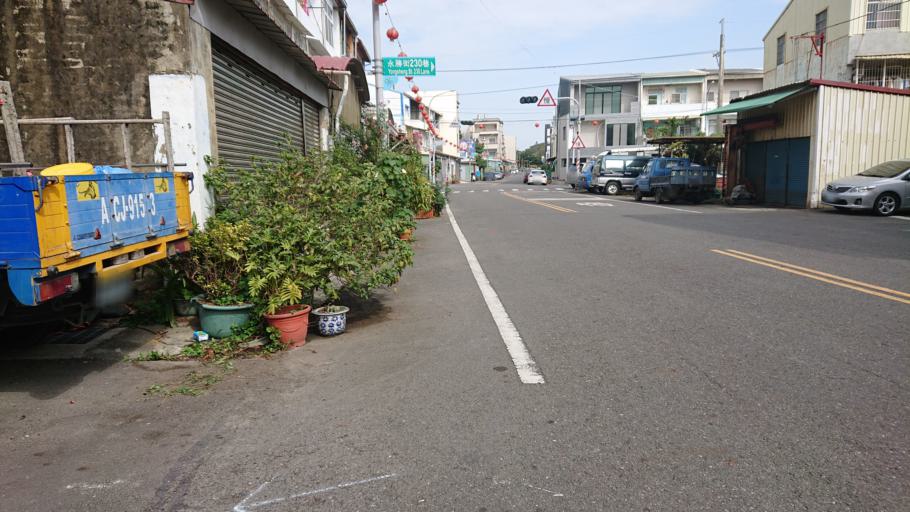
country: TW
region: Taiwan
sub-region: Tainan
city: Tainan
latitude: 23.0186
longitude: 120.2521
